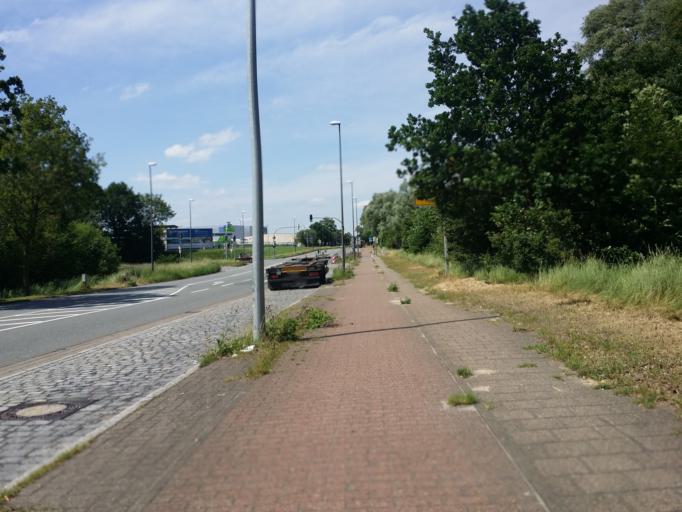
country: DE
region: Lower Saxony
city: Stuhr
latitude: 53.0831
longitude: 8.7514
